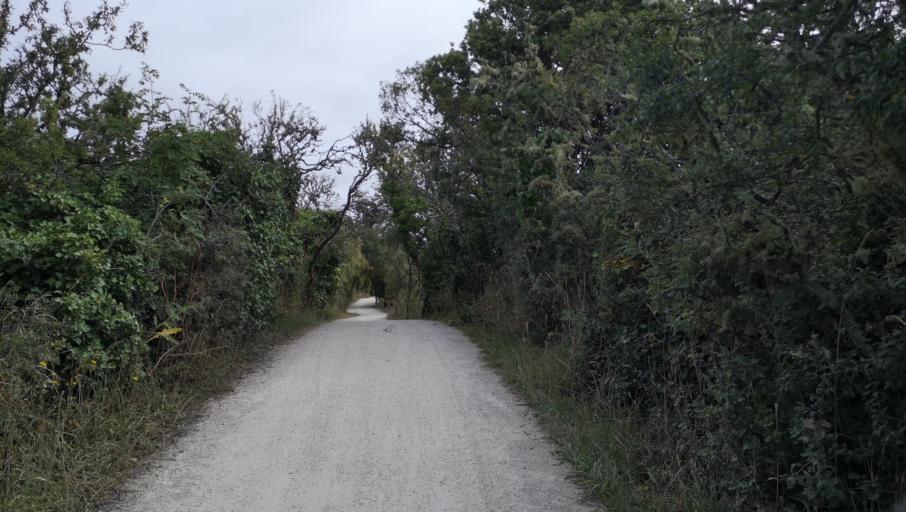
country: FR
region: Pays de la Loire
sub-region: Departement de la Vendee
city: Olonne-sur-Mer
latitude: 46.5305
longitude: -1.8087
